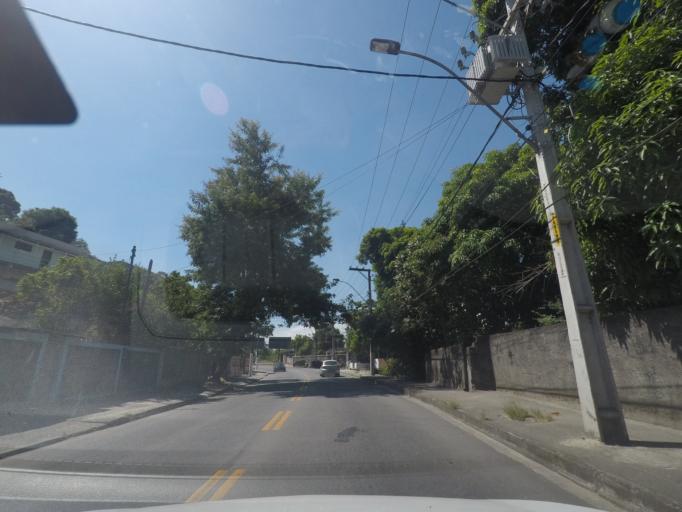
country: BR
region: Rio de Janeiro
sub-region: Niteroi
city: Niteroi
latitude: -22.9113
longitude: -43.0482
